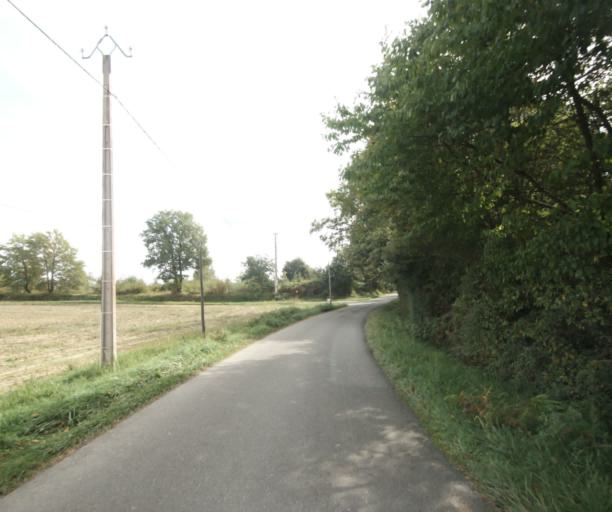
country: FR
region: Midi-Pyrenees
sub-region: Departement du Gers
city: Eauze
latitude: 43.8213
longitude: 0.1247
